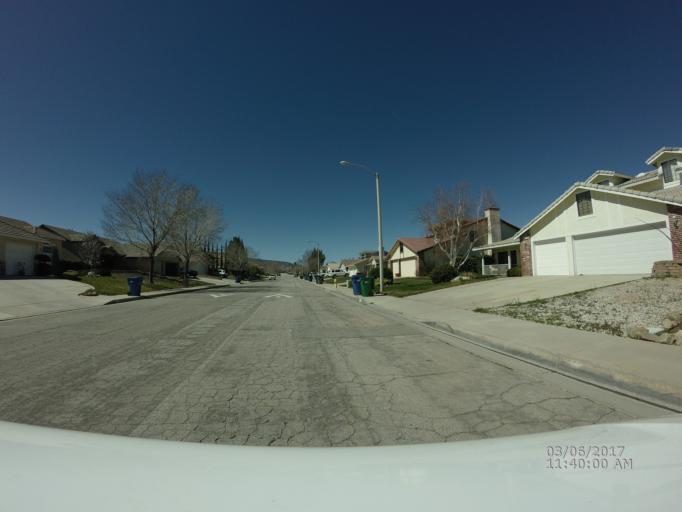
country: US
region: California
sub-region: Los Angeles County
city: Quartz Hill
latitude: 34.6493
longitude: -118.2398
